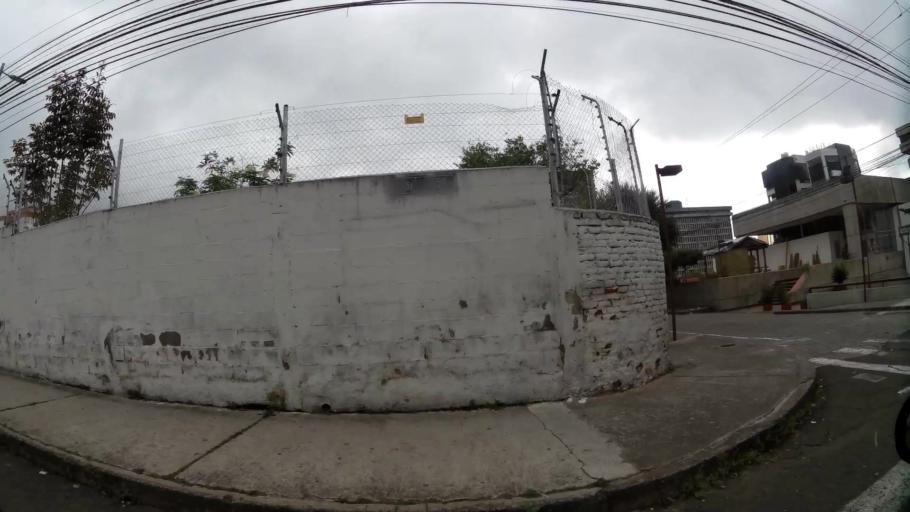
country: EC
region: Pichincha
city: Quito
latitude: -0.1787
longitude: -78.4876
